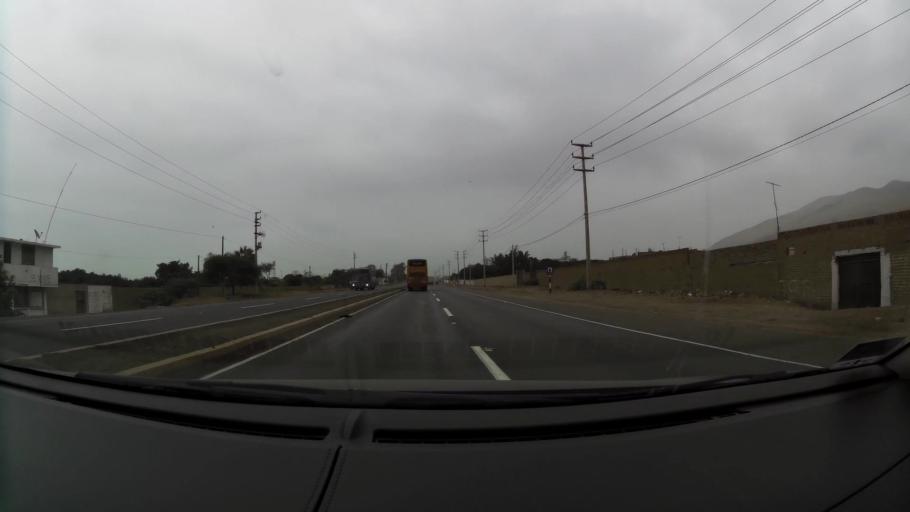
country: PE
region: Lima
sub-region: Provincia de Huaral
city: Chancay
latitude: -11.5715
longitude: -77.2636
